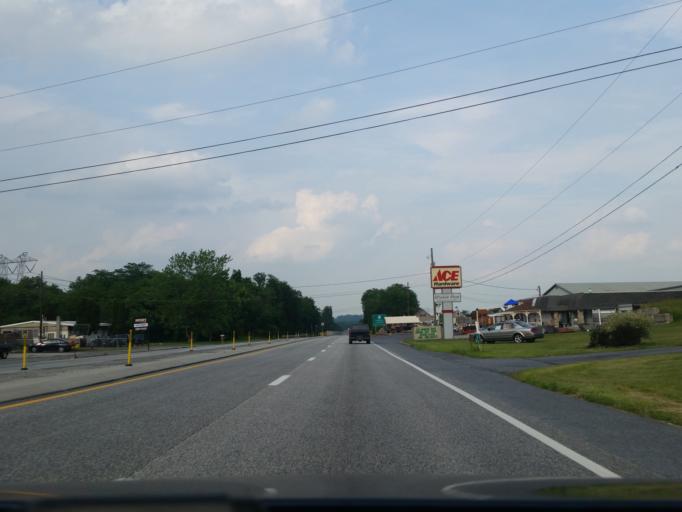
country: US
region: Pennsylvania
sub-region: Lebanon County
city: Jonestown
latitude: 40.4122
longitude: -76.5132
